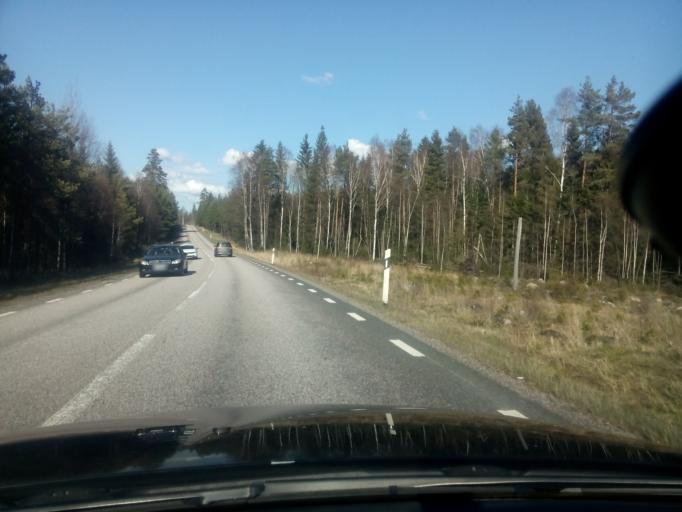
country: SE
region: Soedermanland
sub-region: Strangnas Kommun
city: Akers Styckebruk
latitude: 59.2252
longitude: 16.9209
